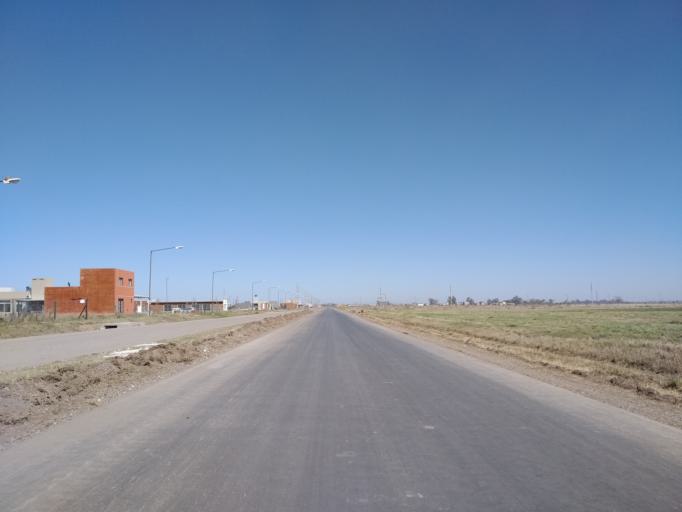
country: AR
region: Santa Fe
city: Funes
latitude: -32.8986
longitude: -60.8056
